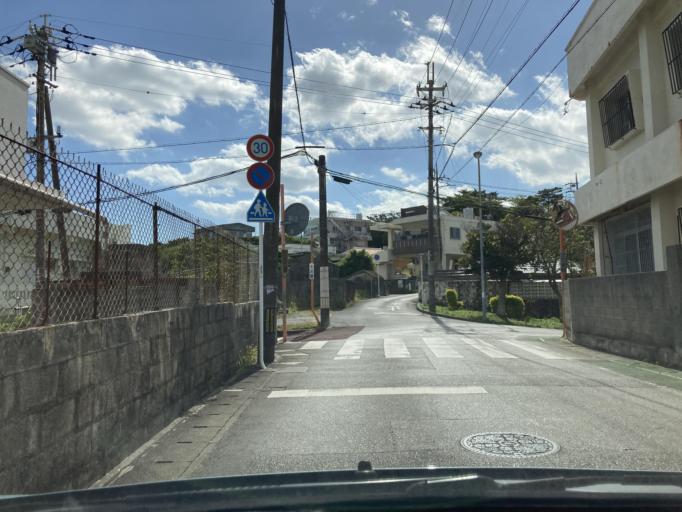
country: JP
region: Okinawa
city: Okinawa
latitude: 26.3418
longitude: 127.8031
